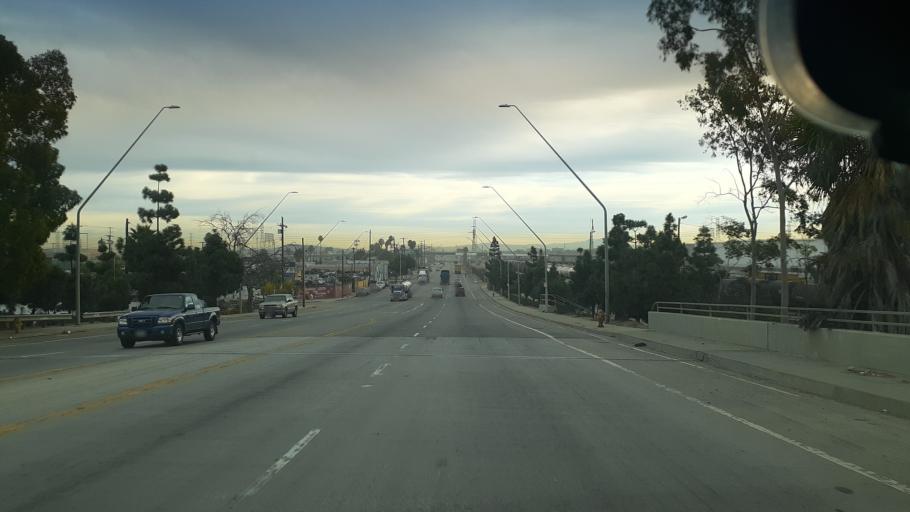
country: US
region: California
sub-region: Los Angeles County
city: Long Beach
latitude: 33.7815
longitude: -118.2357
